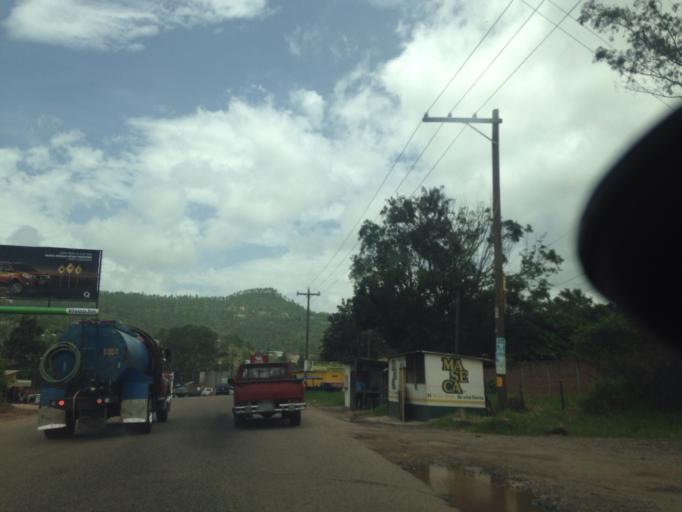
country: HN
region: Francisco Morazan
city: El Tablon
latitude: 14.0448
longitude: -87.1504
